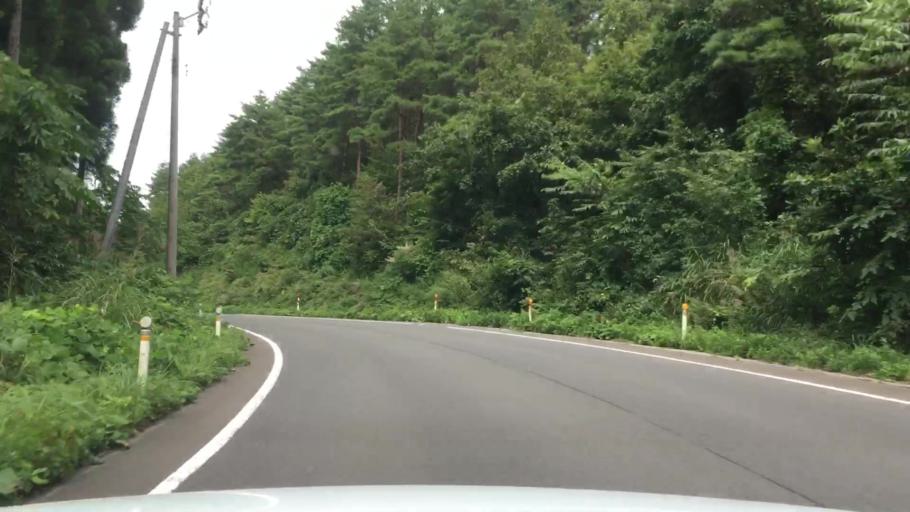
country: JP
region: Aomori
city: Shimokizukuri
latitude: 40.7222
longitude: 140.2583
